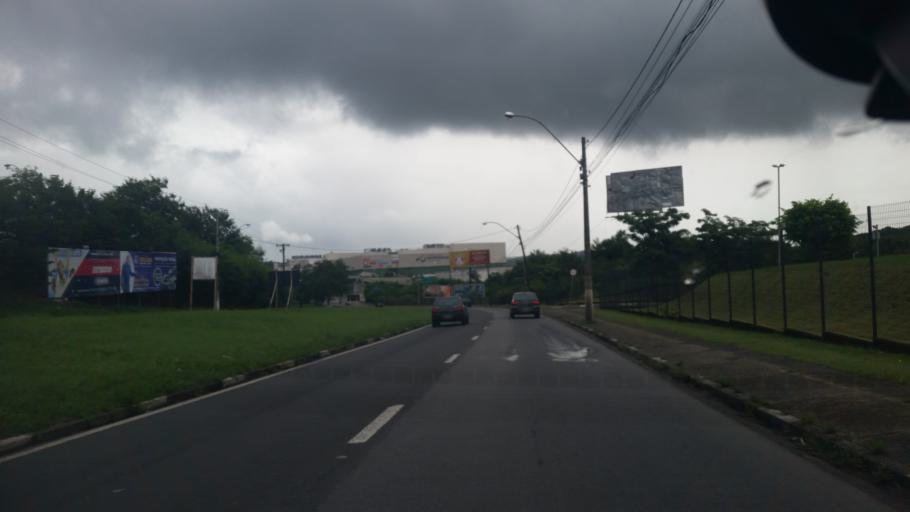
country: BR
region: Sao Paulo
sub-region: Campinas
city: Campinas
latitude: -22.9229
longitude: -47.1215
